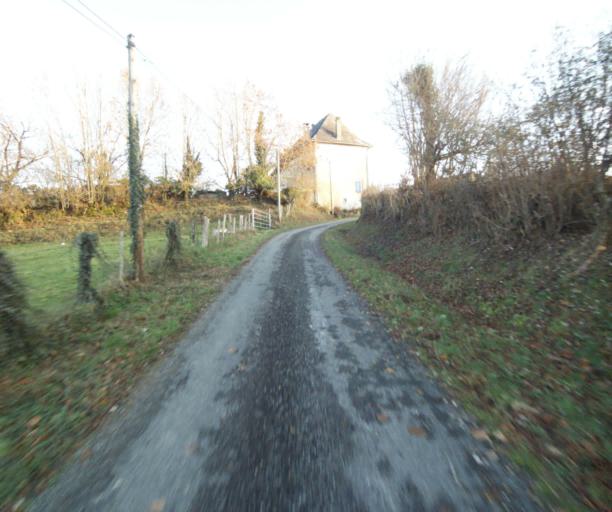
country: FR
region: Limousin
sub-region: Departement de la Correze
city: Laguenne
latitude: 45.2385
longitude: 1.8256
